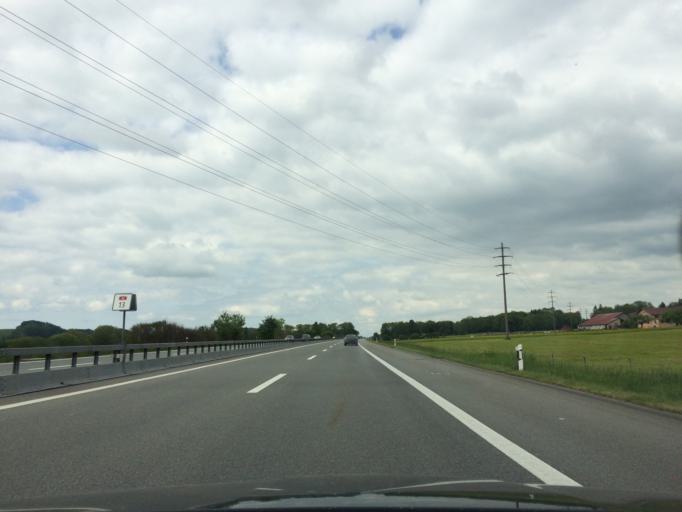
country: CH
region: Fribourg
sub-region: Veveyse District
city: Chatel-Saint-Denis
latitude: 46.5701
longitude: 6.9191
